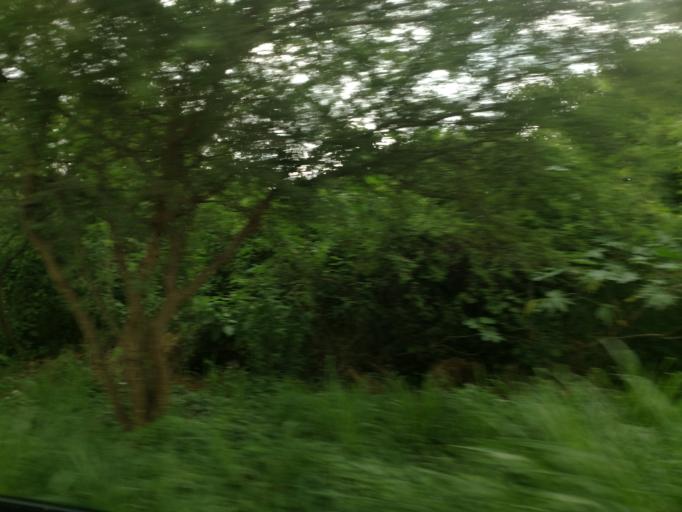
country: MX
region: Nayarit
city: Xalisco
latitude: 21.4765
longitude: -104.8594
